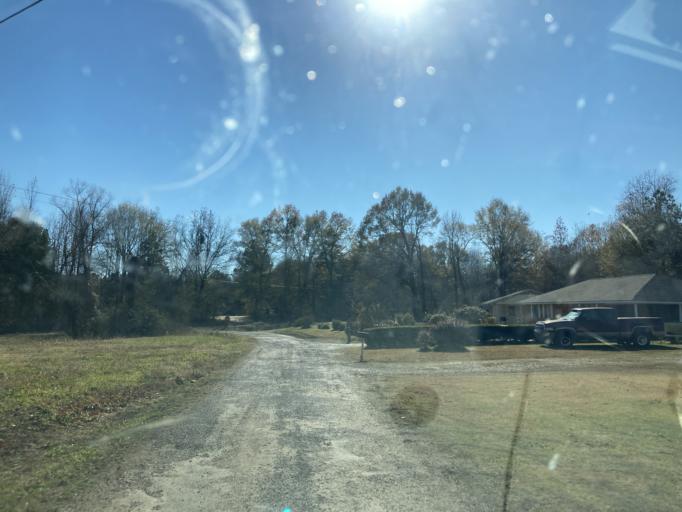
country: US
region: Mississippi
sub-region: Holmes County
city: Pickens
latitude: 32.8554
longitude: -90.0155
